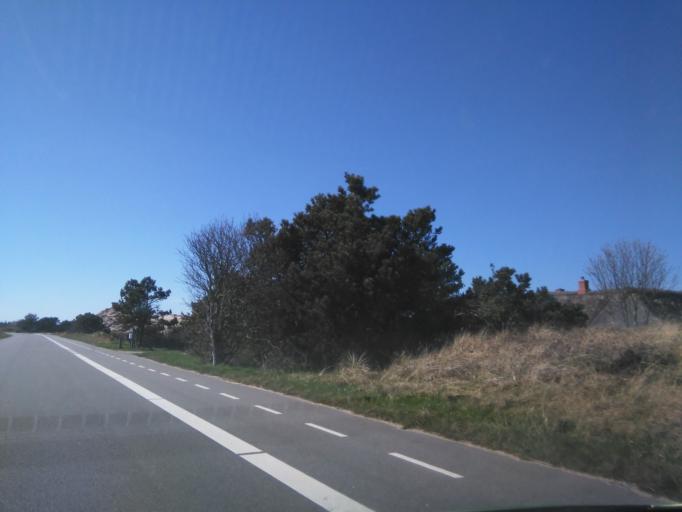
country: DK
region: South Denmark
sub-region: Varde Kommune
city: Oksbol
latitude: 55.5512
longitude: 8.1892
